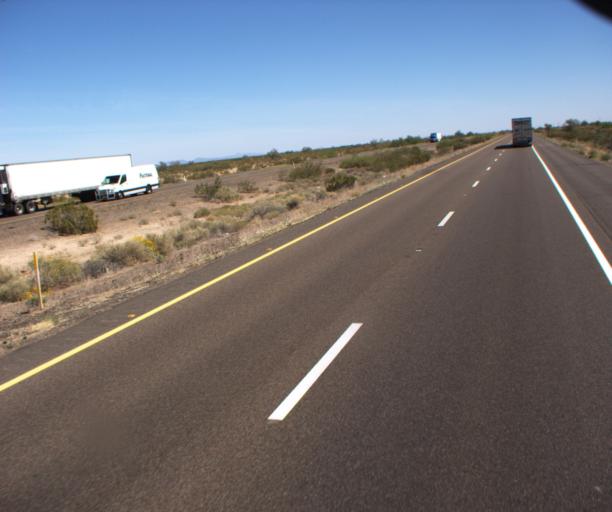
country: US
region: Arizona
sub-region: Yuma County
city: Wellton
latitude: 32.8184
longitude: -113.4892
